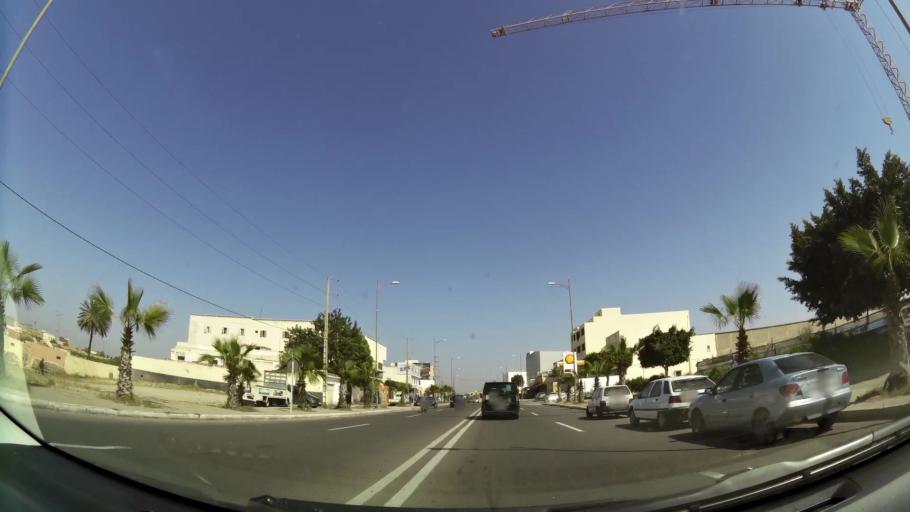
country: MA
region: Souss-Massa-Draa
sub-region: Inezgane-Ait Mellou
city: Inezgane
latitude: 30.3636
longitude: -9.5371
